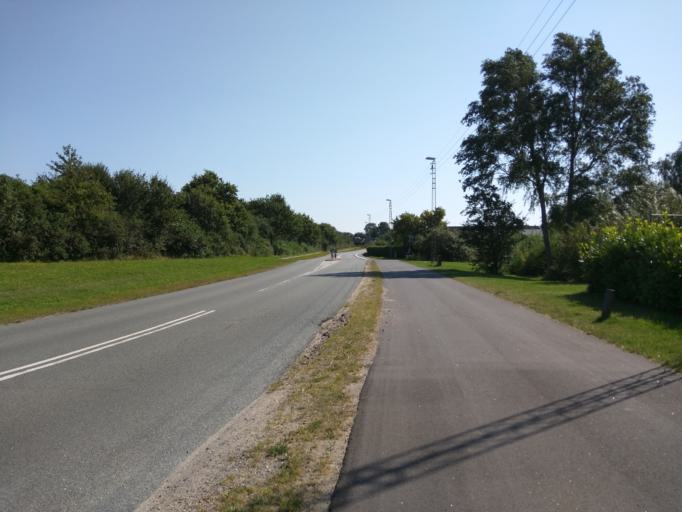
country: DK
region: Central Jutland
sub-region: Viborg Kommune
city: Viborg
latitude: 56.4577
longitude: 9.3744
